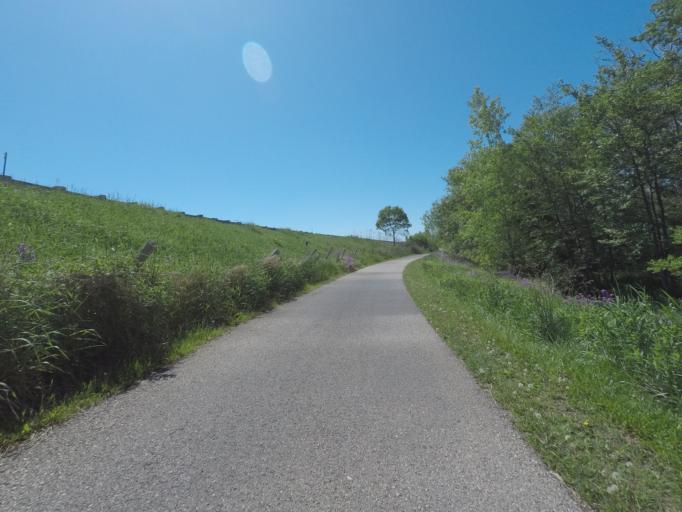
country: US
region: Wisconsin
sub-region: Sheboygan County
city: Kohler
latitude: 43.7503
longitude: -87.7638
